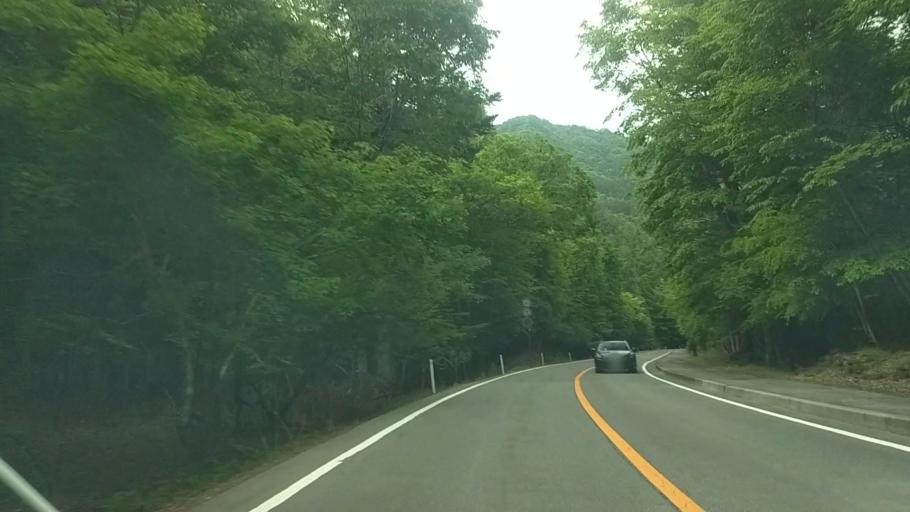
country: JP
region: Yamanashi
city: Fujikawaguchiko
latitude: 35.4942
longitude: 138.6493
